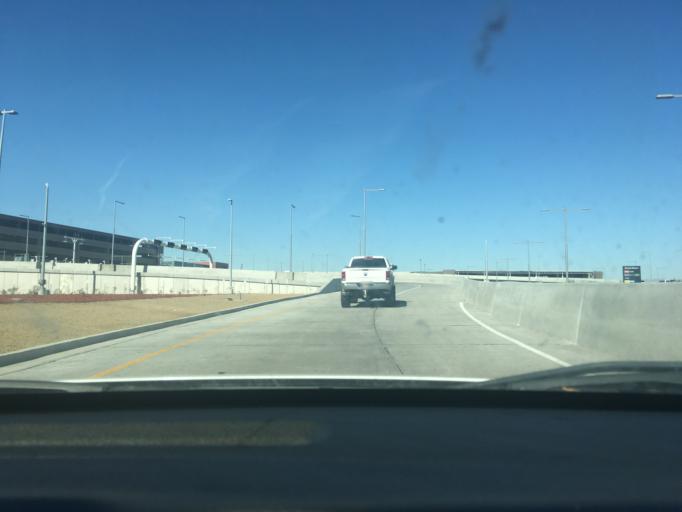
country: US
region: Utah
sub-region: Salt Lake County
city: West Valley City
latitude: 40.7813
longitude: -111.9814
